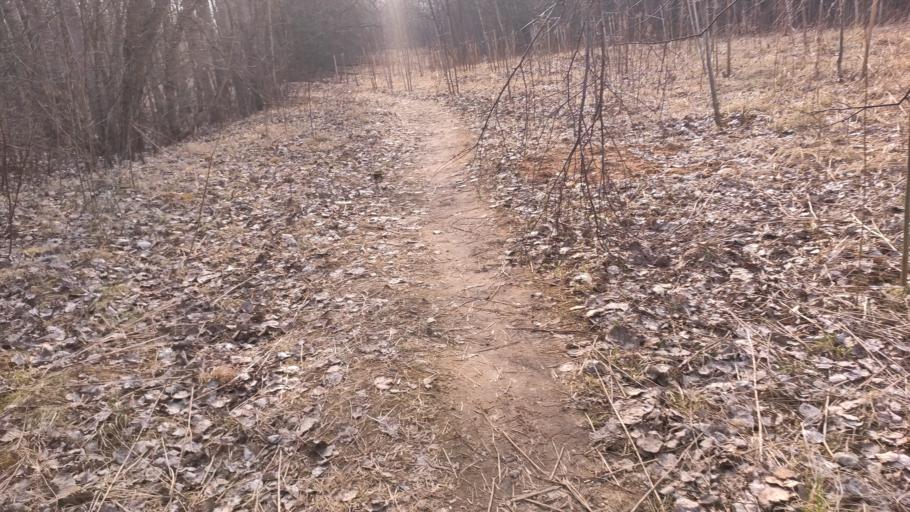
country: BY
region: Minsk
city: Novoye Medvezhino
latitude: 53.8914
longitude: 27.4703
